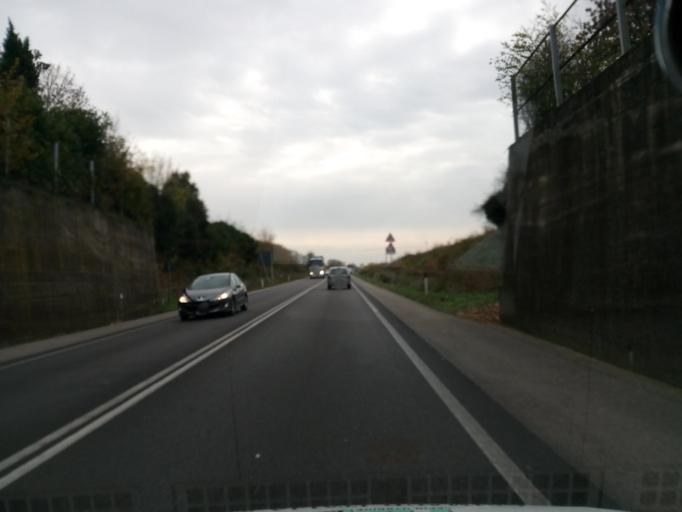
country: IT
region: Veneto
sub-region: Provincia di Treviso
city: Covolo-Levada
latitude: 45.8506
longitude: 12.0080
